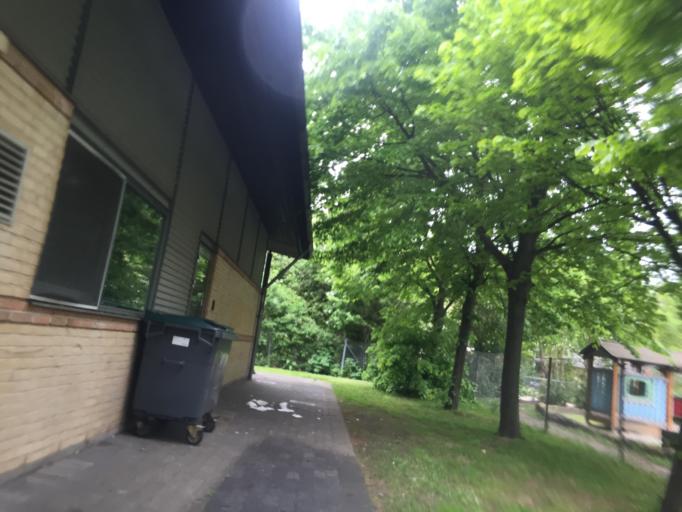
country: DK
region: Capital Region
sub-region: Frederiksberg Kommune
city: Frederiksberg
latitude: 55.6950
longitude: 12.5368
